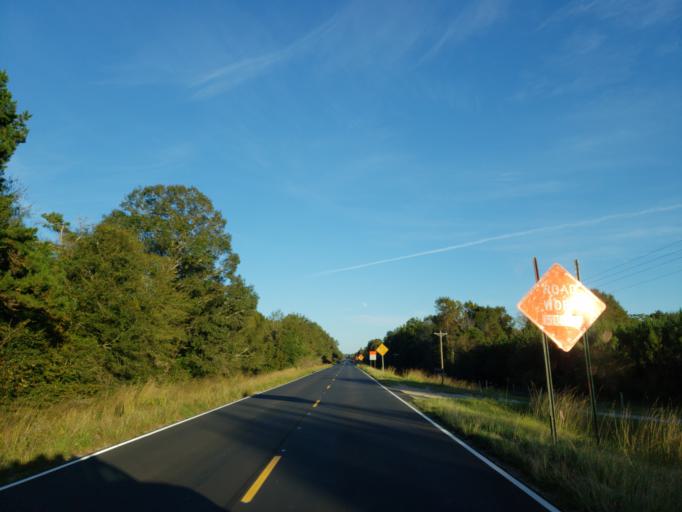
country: US
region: Mississippi
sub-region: Wayne County
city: Belmont
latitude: 31.4240
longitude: -88.5502
